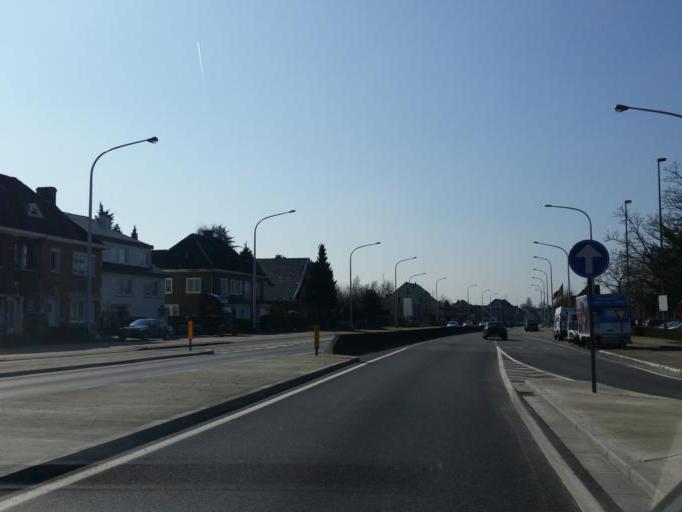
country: BE
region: Flanders
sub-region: Provincie Oost-Vlaanderen
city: Sint-Niklaas
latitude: 51.1559
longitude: 4.1541
